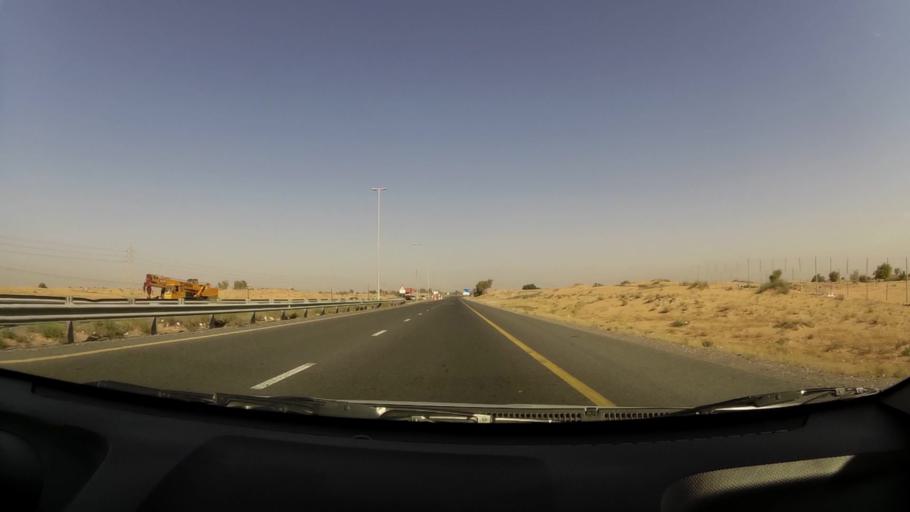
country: AE
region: Umm al Qaywayn
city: Umm al Qaywayn
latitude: 25.4627
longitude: 55.6004
